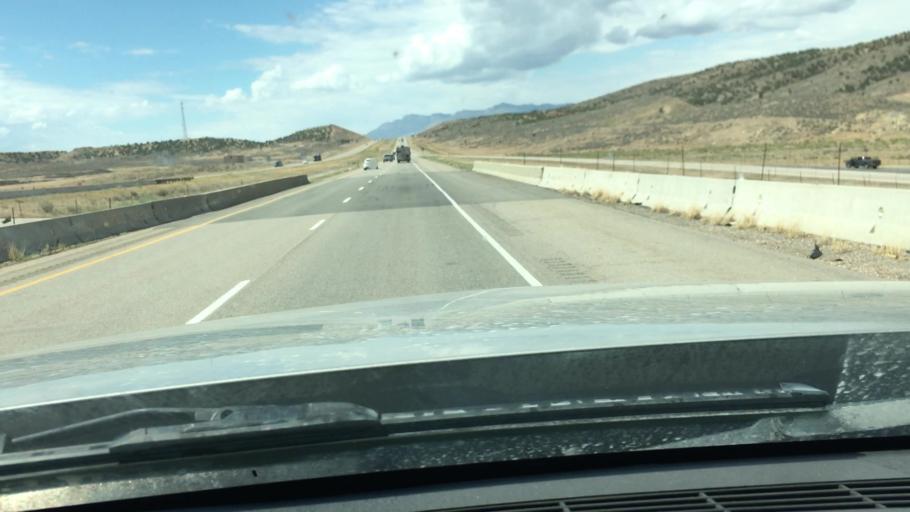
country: US
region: Utah
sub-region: Juab County
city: Nephi
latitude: 39.4839
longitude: -111.9785
